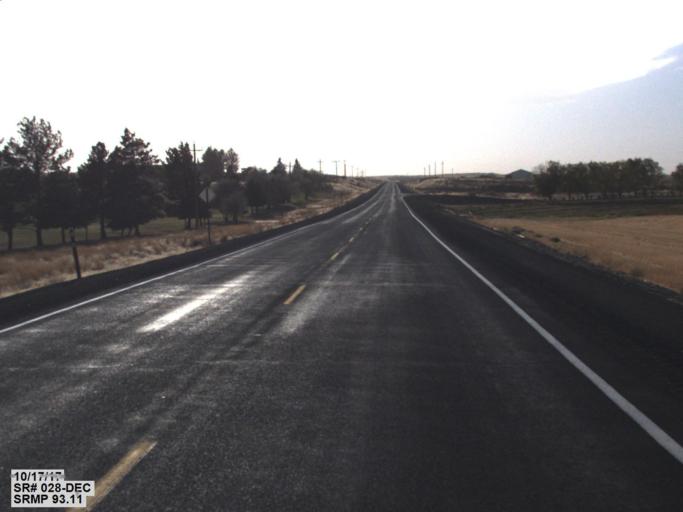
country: US
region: Washington
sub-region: Adams County
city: Ritzville
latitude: 47.3308
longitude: -118.7043
